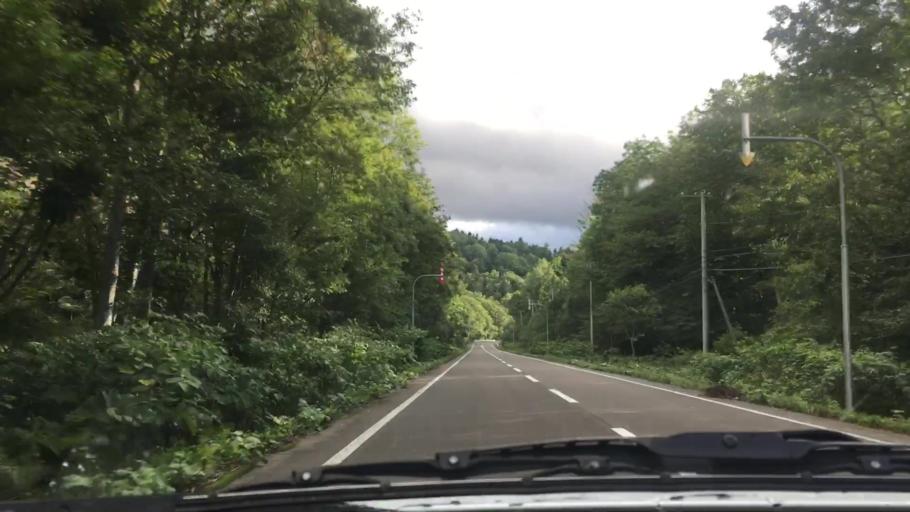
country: JP
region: Hokkaido
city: Shimo-furano
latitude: 43.0894
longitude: 142.6809
